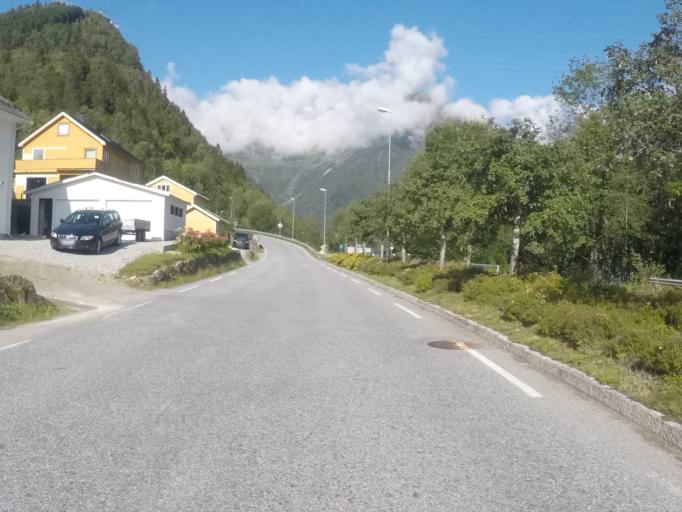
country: NO
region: Sogn og Fjordane
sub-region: Balestrand
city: Balestrand
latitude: 61.2103
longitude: 6.5326
